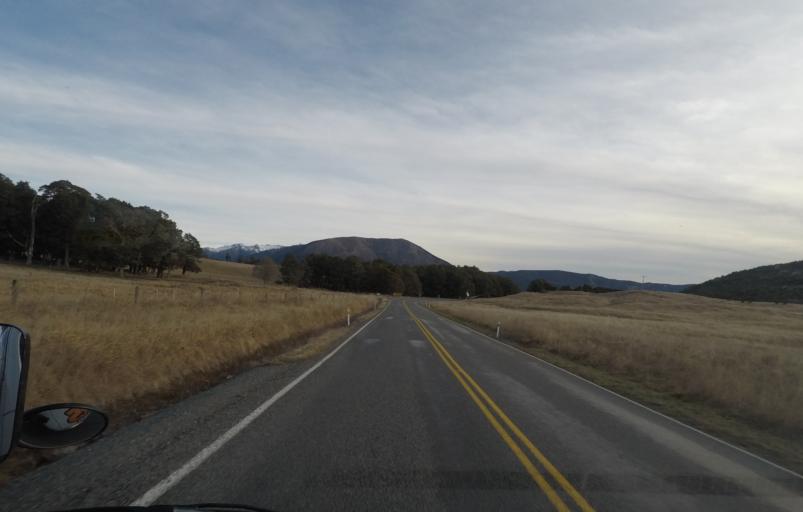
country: NZ
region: Tasman
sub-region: Tasman District
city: Wakefield
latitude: -41.7986
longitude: 172.8692
